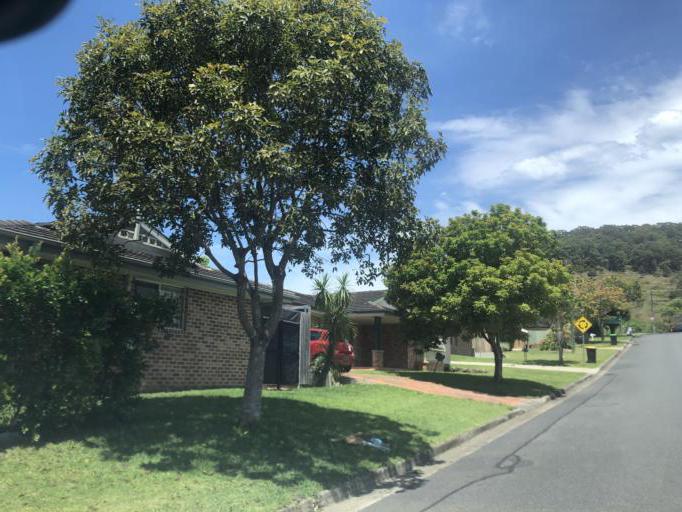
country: AU
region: New South Wales
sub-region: Coffs Harbour
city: Coffs Harbour
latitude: -30.2899
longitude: 153.0971
